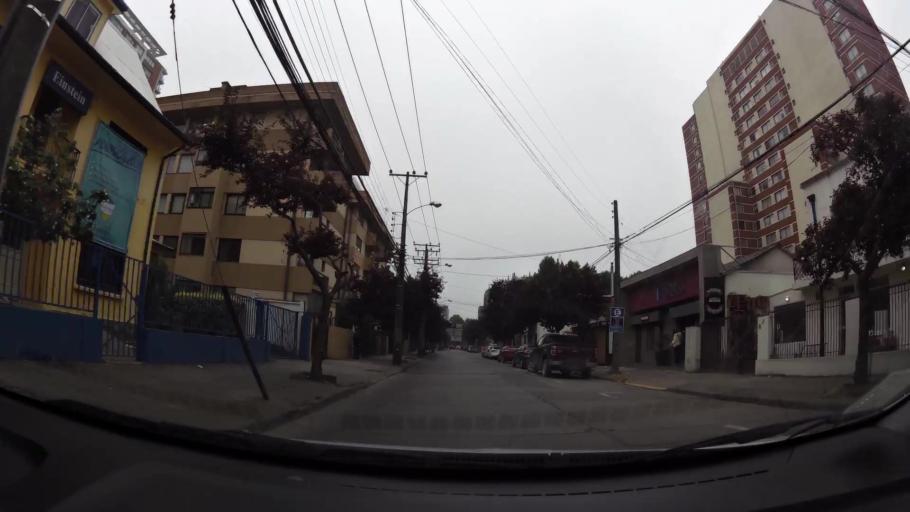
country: CL
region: Biobio
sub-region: Provincia de Concepcion
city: Concepcion
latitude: -36.8283
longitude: -73.0407
